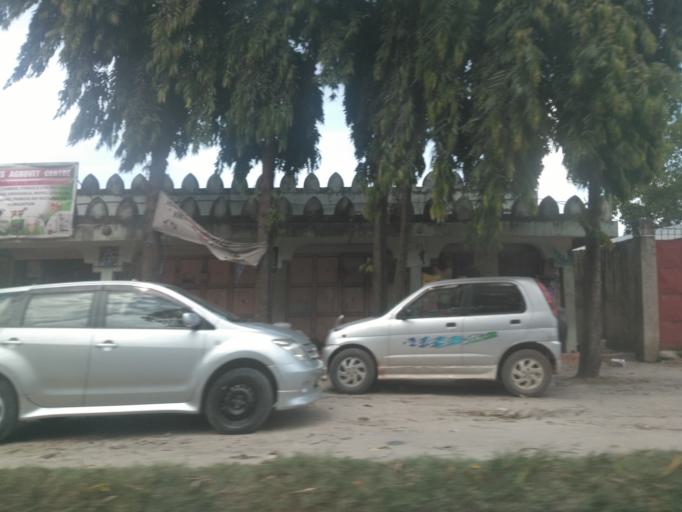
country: TZ
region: Zanzibar Urban/West
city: Zanzibar
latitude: -6.1548
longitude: 39.2069
